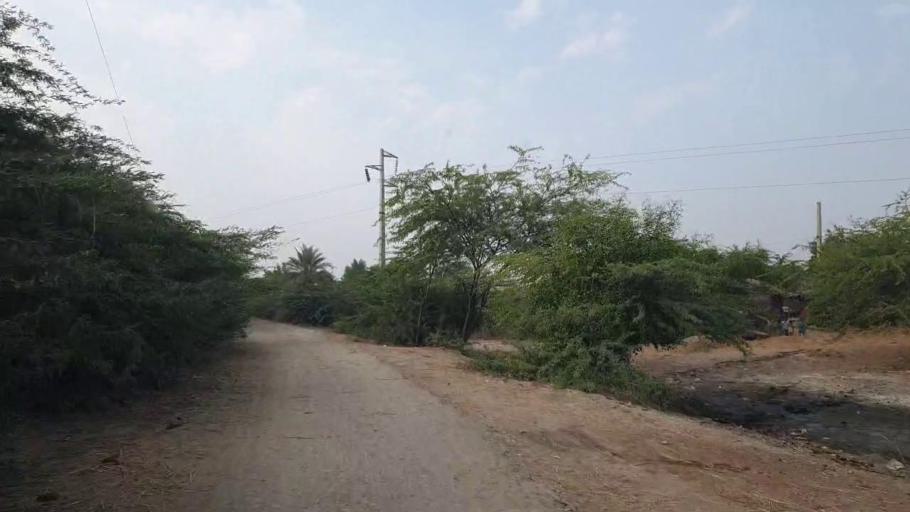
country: PK
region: Sindh
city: Talhar
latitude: 24.8472
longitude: 68.8142
